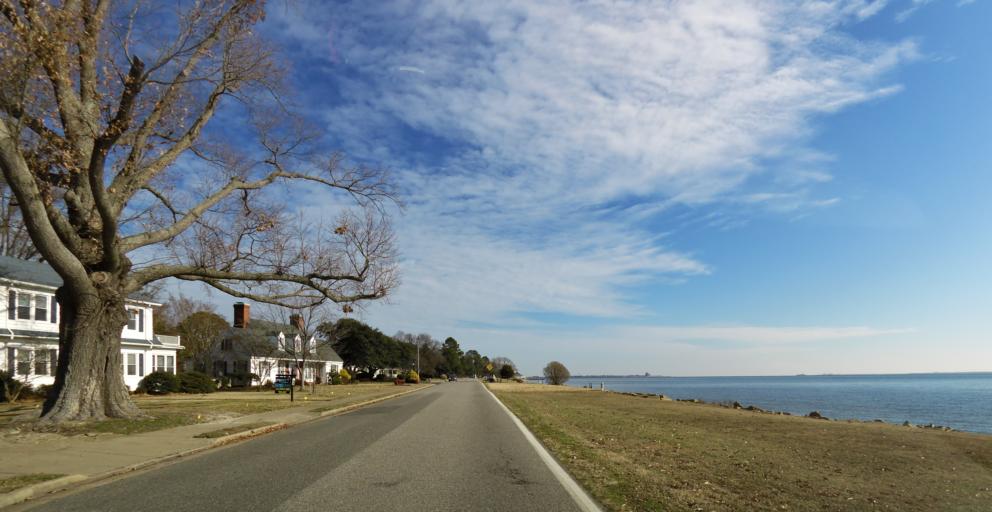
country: US
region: Virginia
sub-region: City of Hampton
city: Hampton
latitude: 37.0015
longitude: -76.3653
